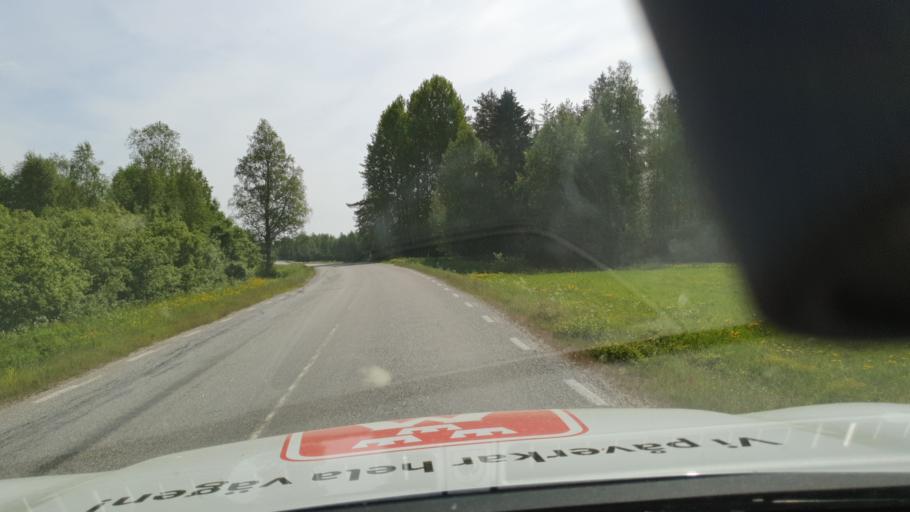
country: SE
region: Vaesterbotten
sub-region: Robertsfors Kommun
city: Robertsfors
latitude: 64.2844
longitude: 20.9368
